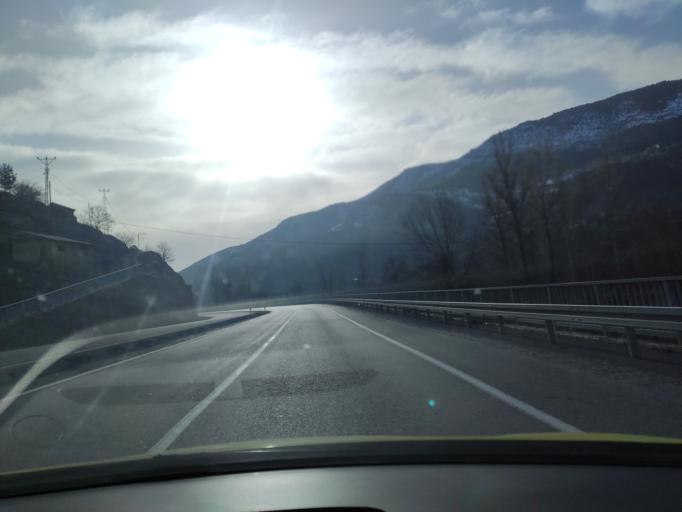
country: TR
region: Gumushane
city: Kale
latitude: 40.4038
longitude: 39.6213
